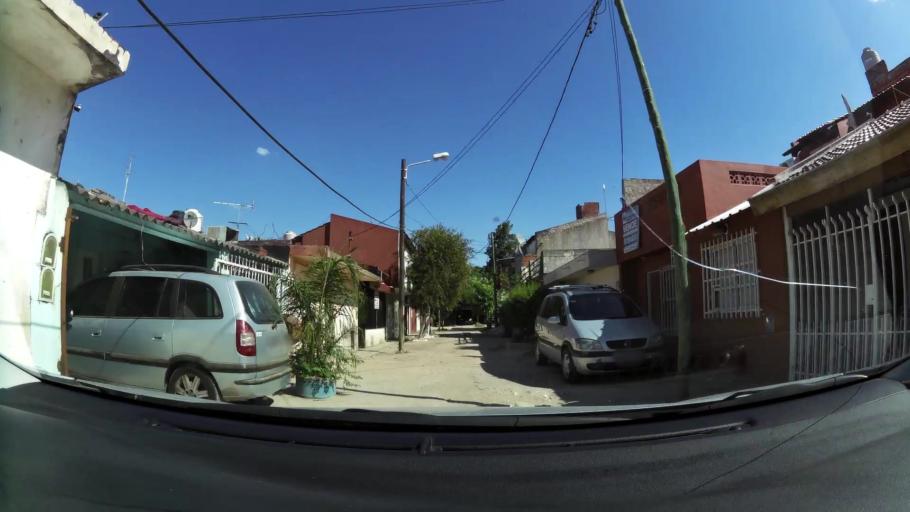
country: AR
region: Buenos Aires F.D.
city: Villa Lugano
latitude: -34.7074
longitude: -58.4769
